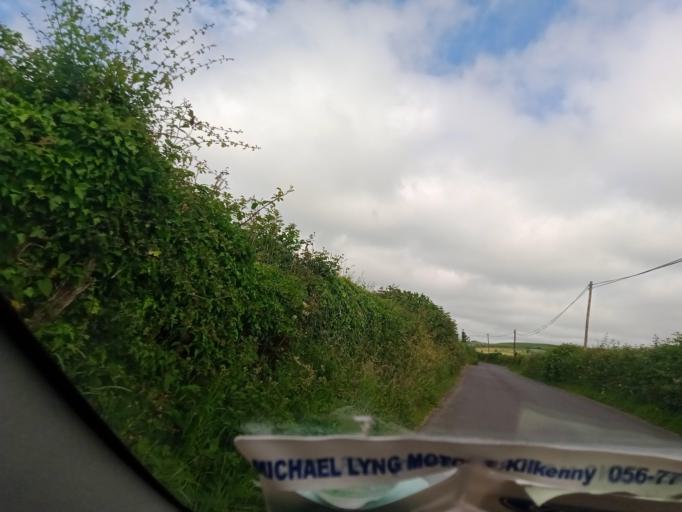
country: IE
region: Leinster
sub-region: Kilkenny
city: Ballyragget
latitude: 52.7629
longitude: -7.4590
